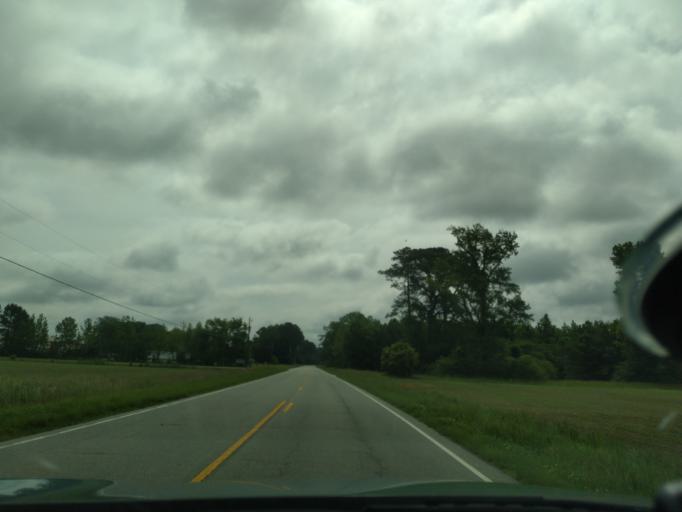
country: US
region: North Carolina
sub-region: Washington County
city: Plymouth
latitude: 35.8755
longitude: -76.6357
